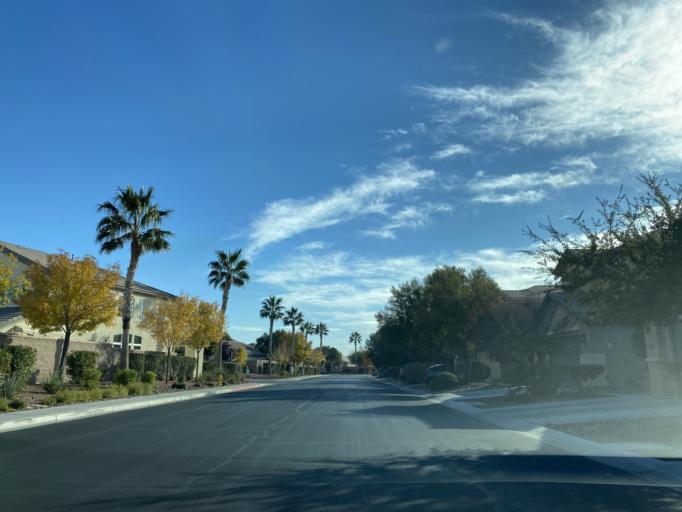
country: US
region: Nevada
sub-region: Clark County
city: North Las Vegas
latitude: 36.3198
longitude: -115.2433
